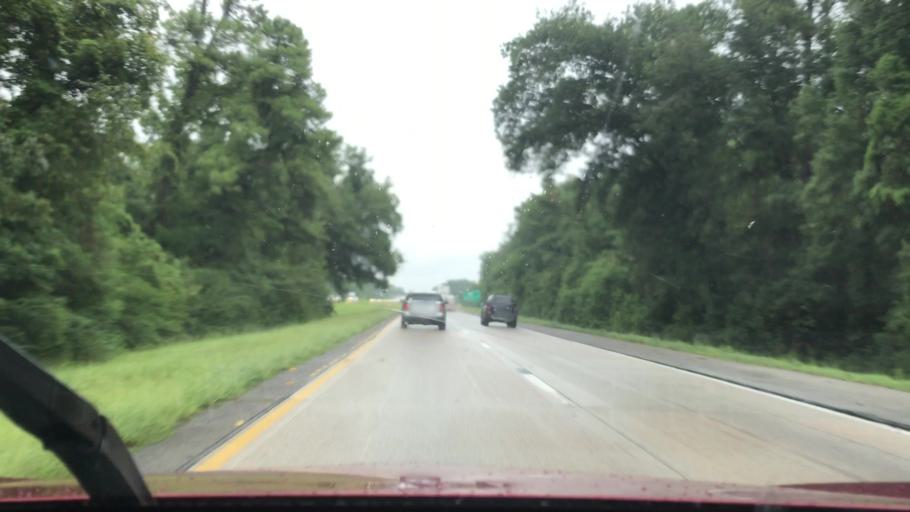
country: US
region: South Carolina
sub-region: Orangeburg County
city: Holly Hill
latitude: 33.2348
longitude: -80.4530
